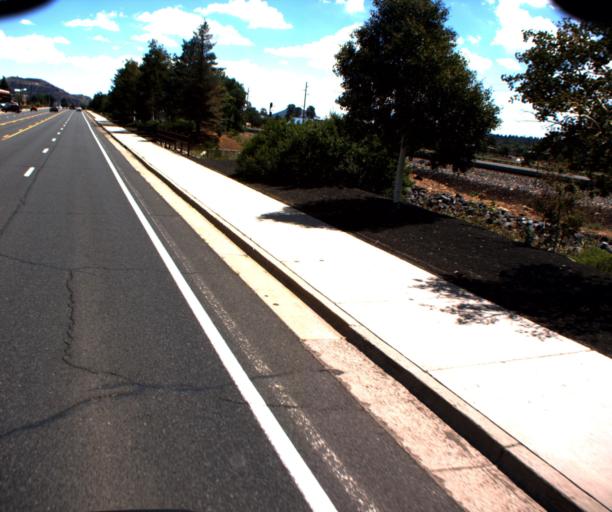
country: US
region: Arizona
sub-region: Coconino County
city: Flagstaff
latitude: 35.2124
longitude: -111.6017
